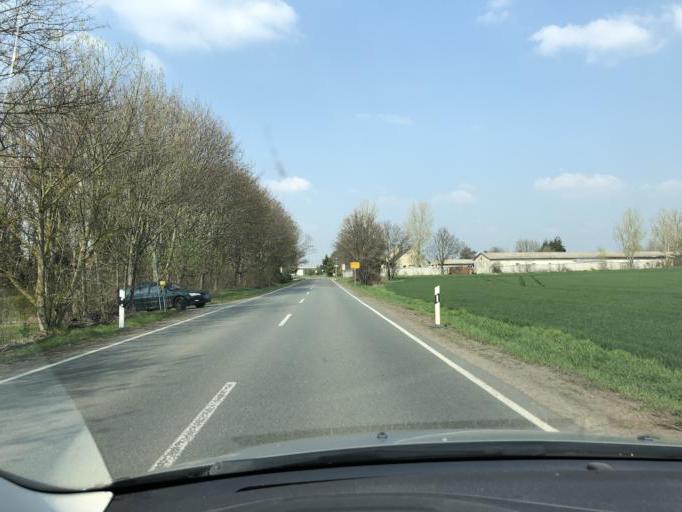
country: DE
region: Saxony-Anhalt
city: Zorbig
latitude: 51.5821
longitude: 12.1412
